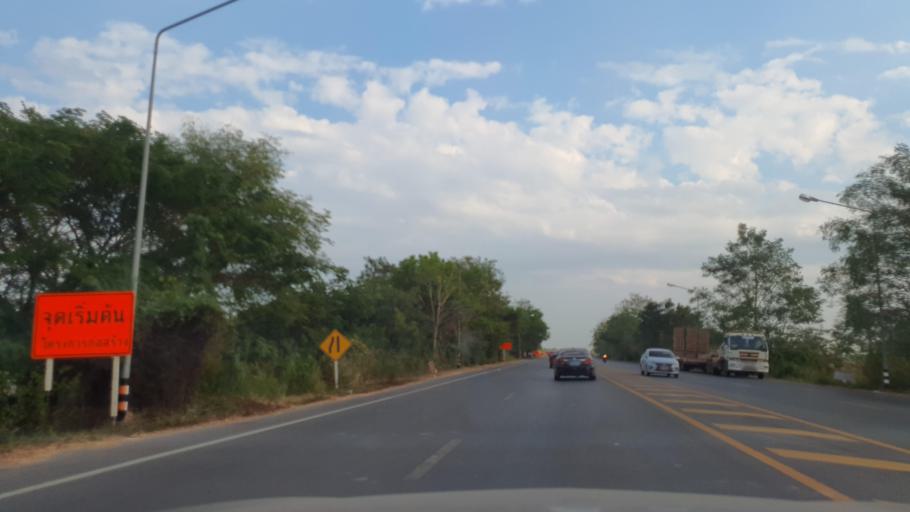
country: TH
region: Nakhon Phanom
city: Ban Phaeng
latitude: 17.9470
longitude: 104.2232
